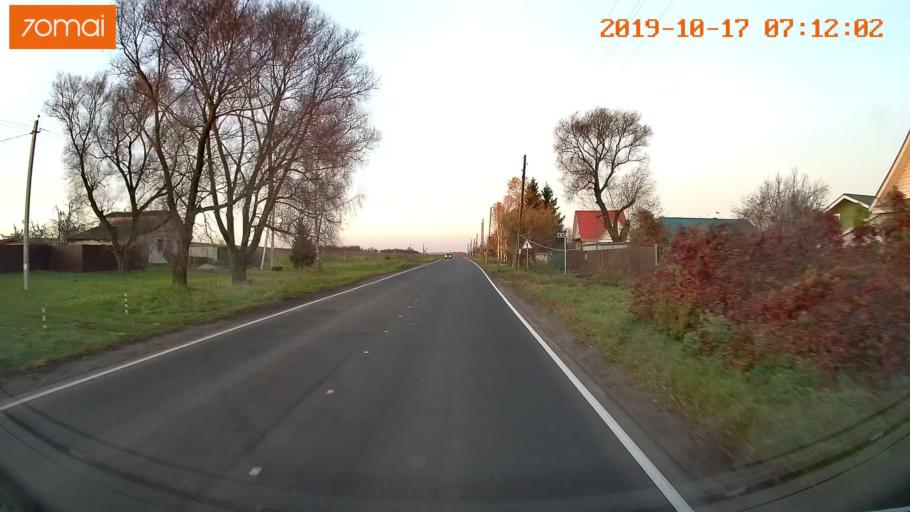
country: RU
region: Vladimir
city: Suzdal'
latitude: 56.4022
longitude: 40.3373
